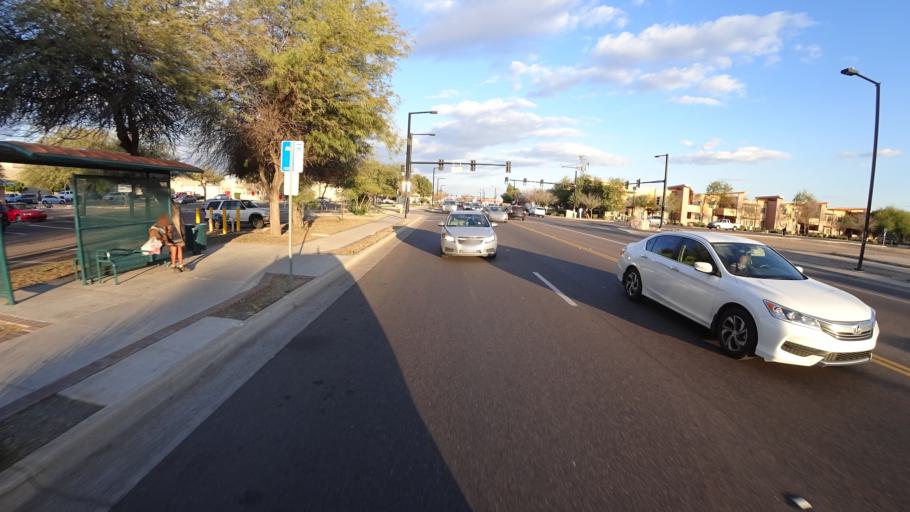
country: US
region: Arizona
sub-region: Maricopa County
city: Glendale
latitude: 33.5385
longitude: -112.1955
